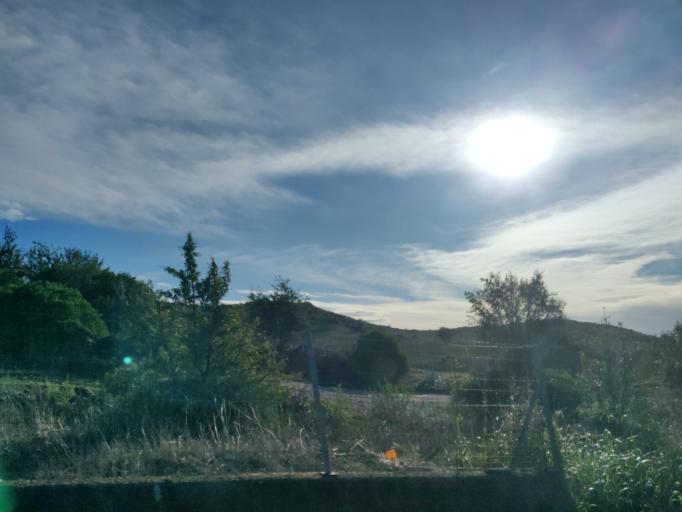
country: IT
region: Tuscany
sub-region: Provincia di Grosseto
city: Gavorrano
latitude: 42.9385
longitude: 10.9444
